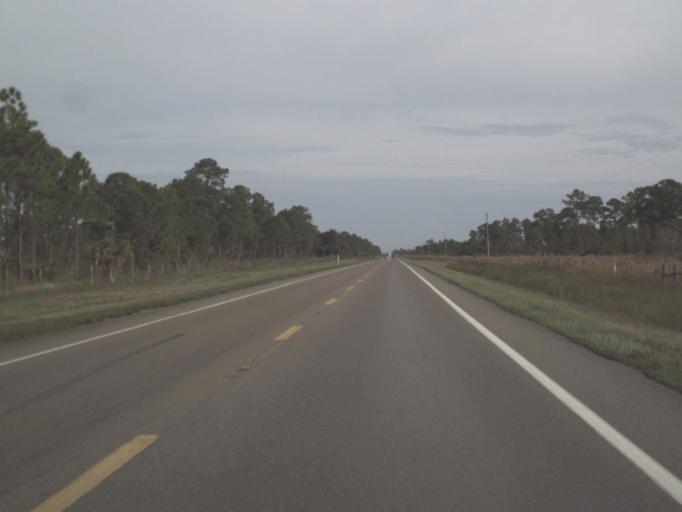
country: US
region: Florida
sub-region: Lee County
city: Olga
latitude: 26.8403
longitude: -81.7598
